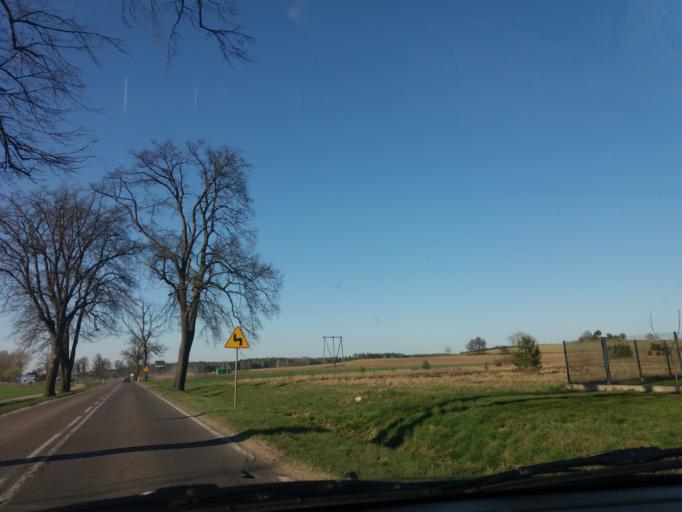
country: PL
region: Warmian-Masurian Voivodeship
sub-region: Powiat nidzicki
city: Nidzica
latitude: 53.3781
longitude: 20.4311
